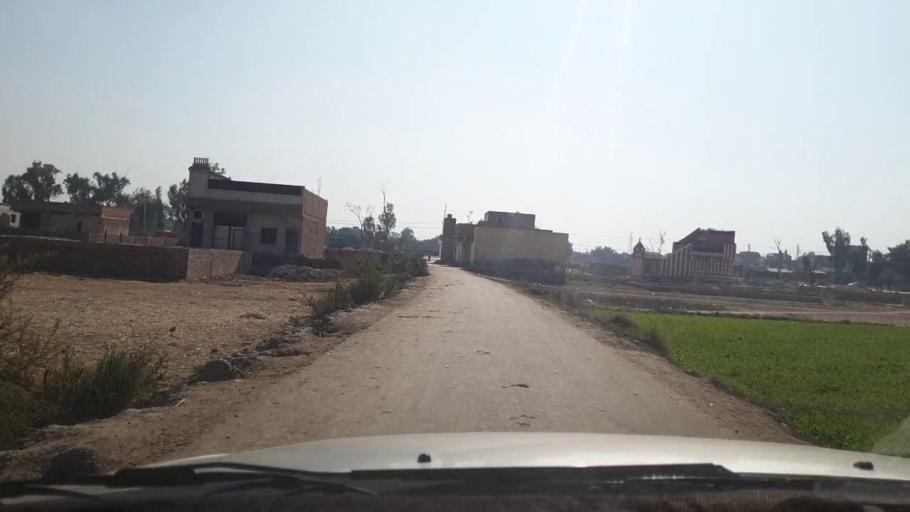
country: PK
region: Sindh
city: Mirpur Mathelo
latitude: 28.0305
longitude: 69.5510
